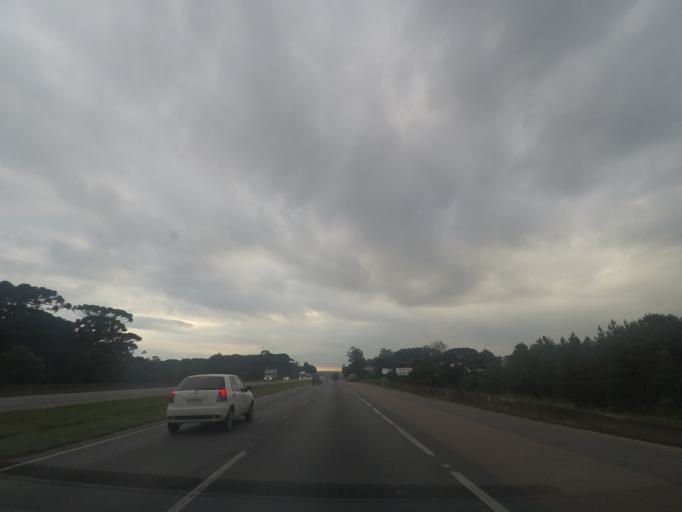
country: BR
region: Parana
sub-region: Sao Jose Dos Pinhais
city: Sao Jose dos Pinhais
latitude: -25.5716
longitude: -49.2068
